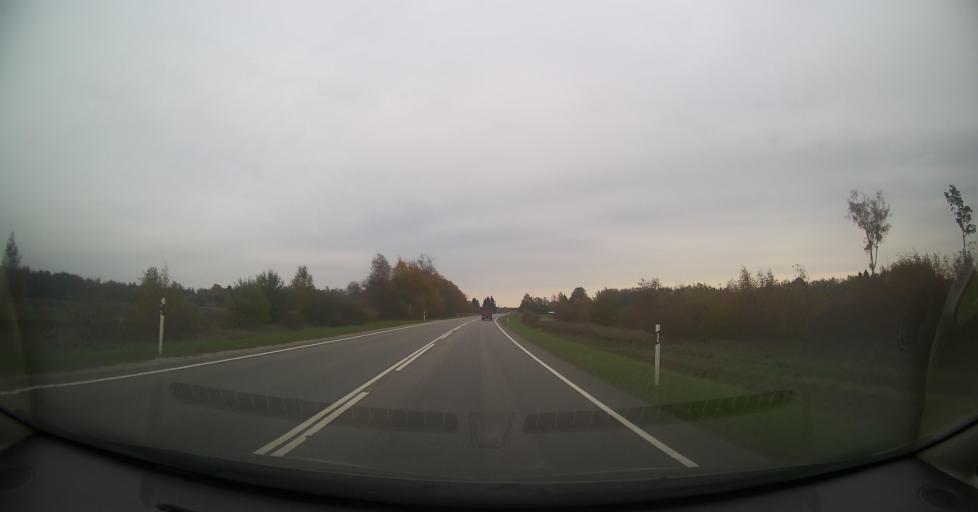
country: EE
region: Laeaene
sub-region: Ridala Parish
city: Uuemoisa
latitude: 58.9741
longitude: 23.8533
